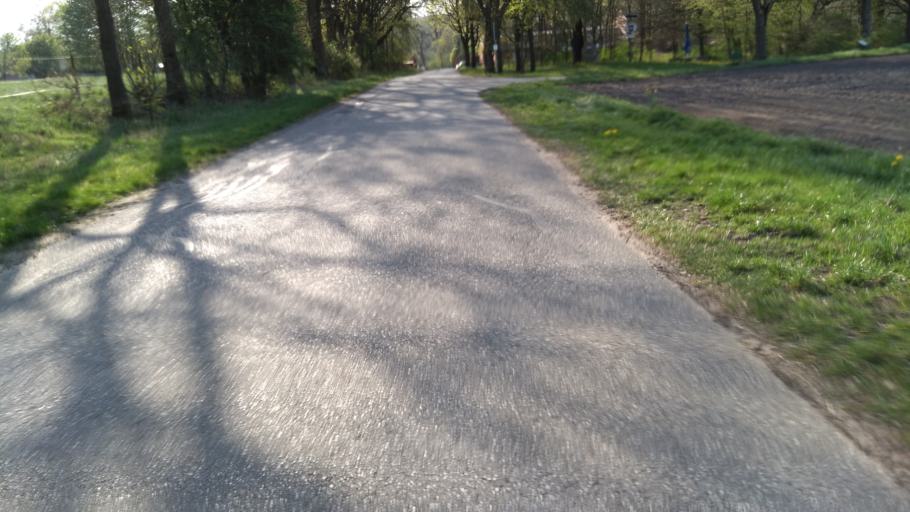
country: DE
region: Lower Saxony
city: Buxtehude
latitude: 53.4369
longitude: 9.6784
